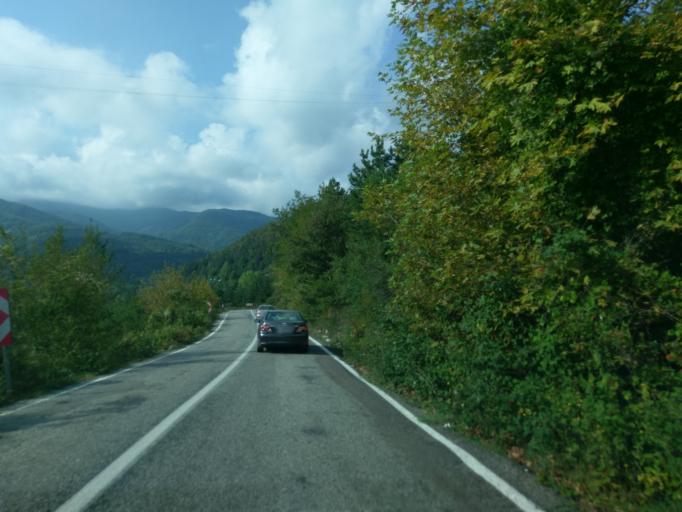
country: TR
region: Sinop
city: Yenikonak
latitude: 41.8763
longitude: 34.5456
